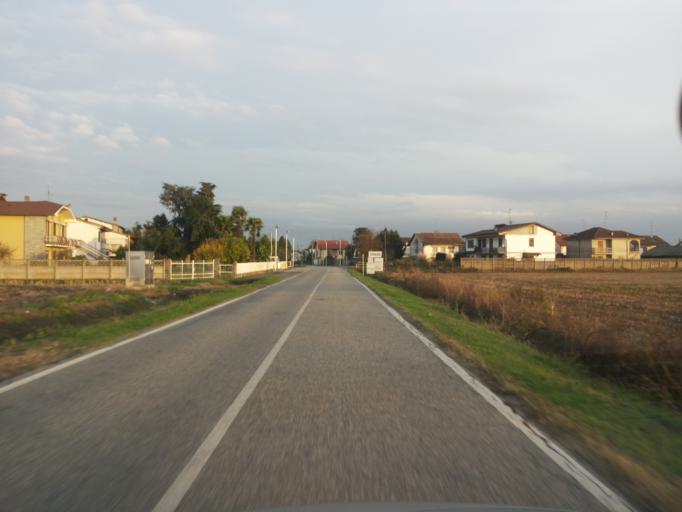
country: IT
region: Piedmont
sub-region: Provincia di Vercelli
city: Costanzana
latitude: 45.2396
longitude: 8.3637
